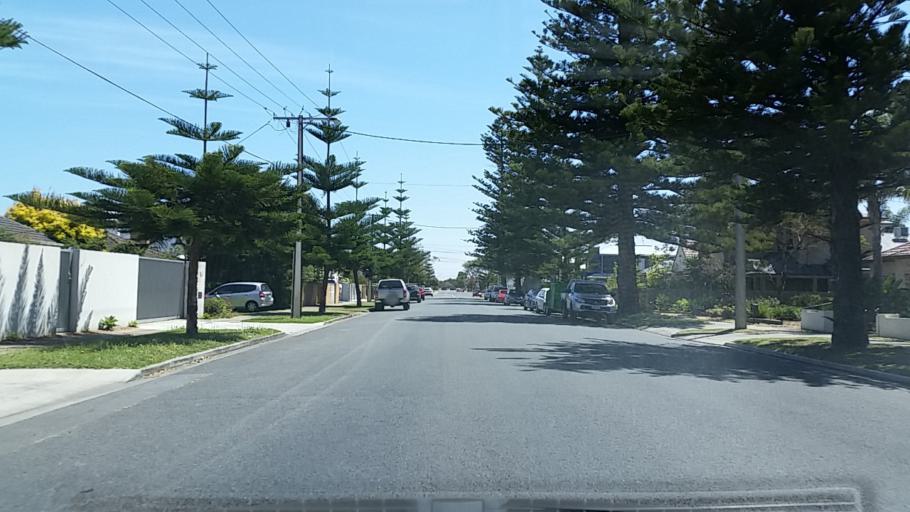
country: AU
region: South Australia
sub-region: Charles Sturt
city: Grange
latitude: -34.9013
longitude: 138.4924
